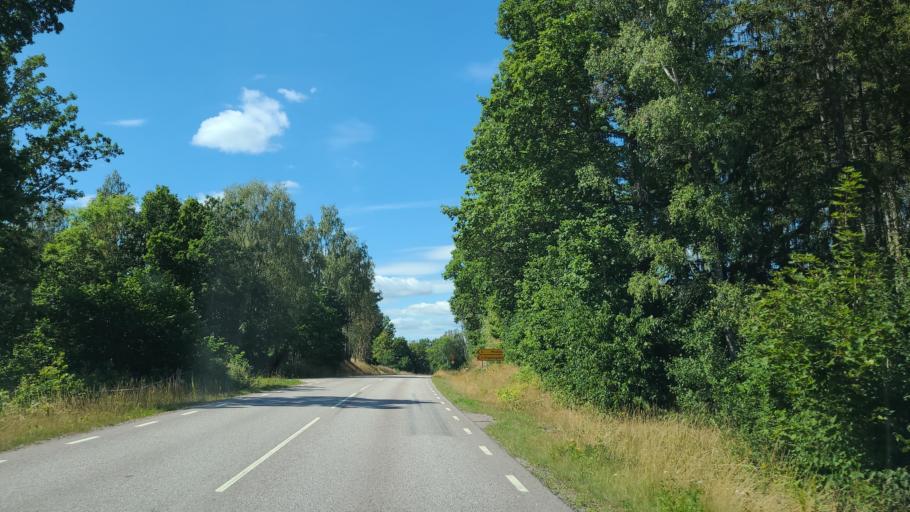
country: SE
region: Kalmar
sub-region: Emmaboda Kommun
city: Emmaboda
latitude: 56.5343
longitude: 15.6562
